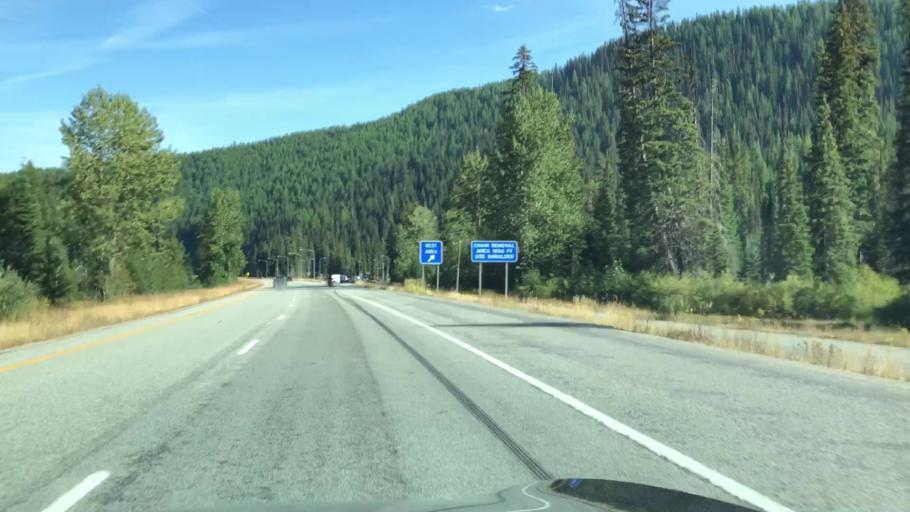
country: US
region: Idaho
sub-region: Shoshone County
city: Wallace
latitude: 47.4221
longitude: -115.6336
